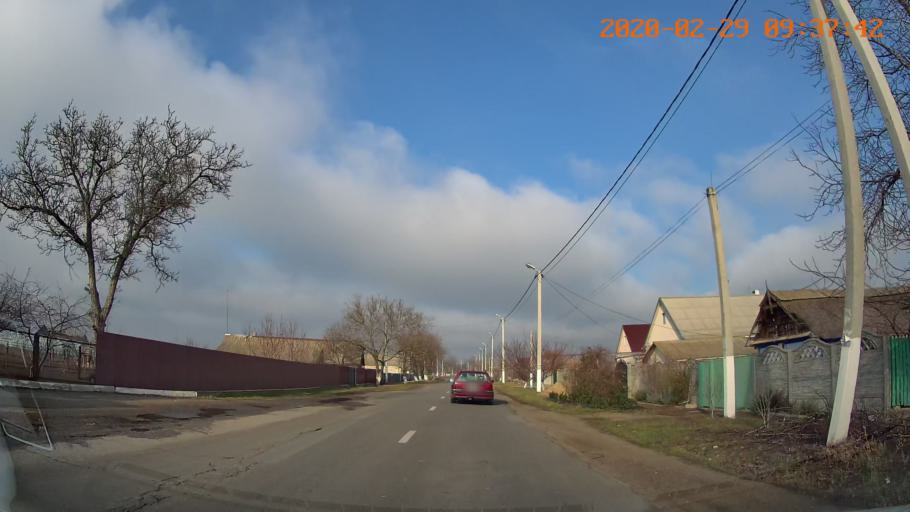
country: MD
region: Telenesti
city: Dnestrovsc
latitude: 46.6285
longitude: 29.8744
